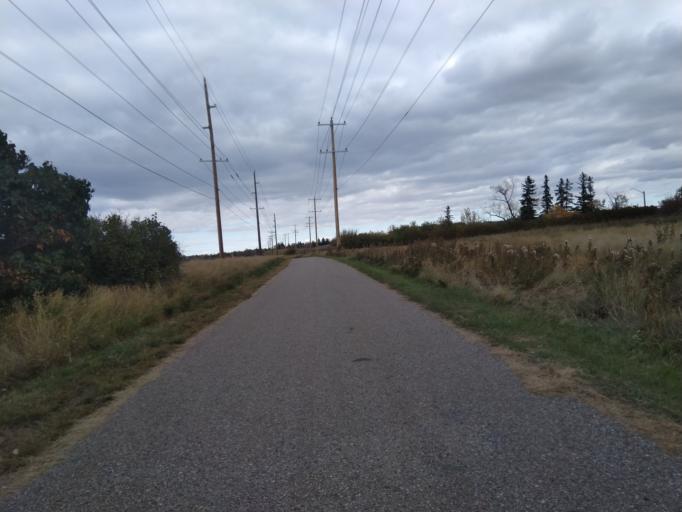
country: CA
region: Alberta
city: Calgary
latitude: 51.0255
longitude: -113.9981
